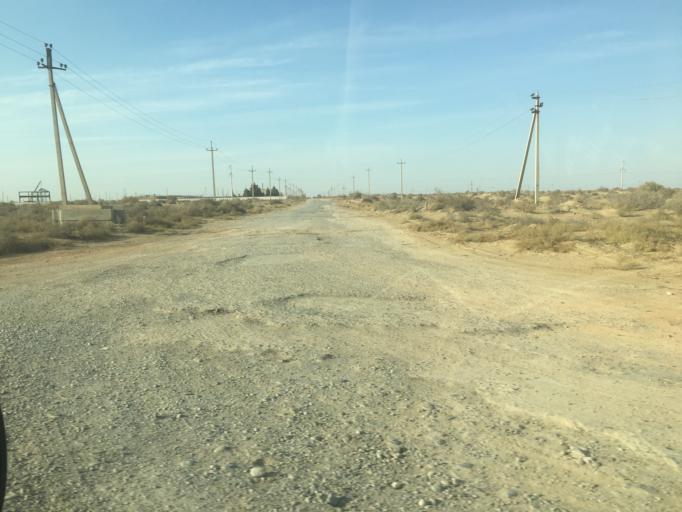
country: TM
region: Mary
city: Mary
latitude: 37.5873
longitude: 61.5355
